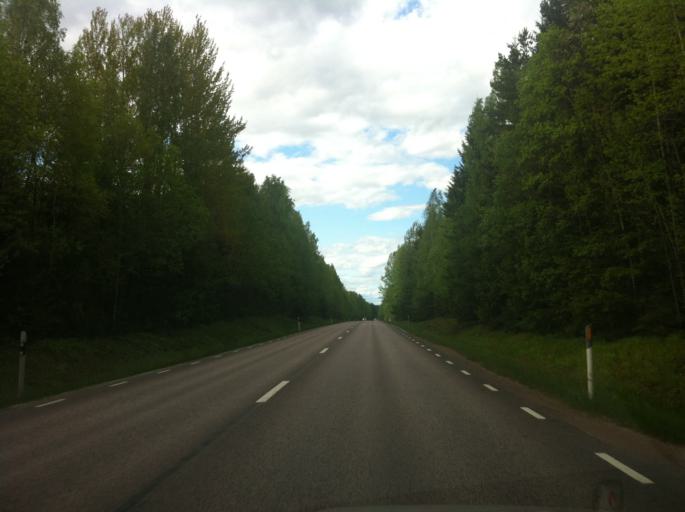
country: SE
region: Vaermland
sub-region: Storfors Kommun
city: Storfors
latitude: 59.5885
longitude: 14.2593
